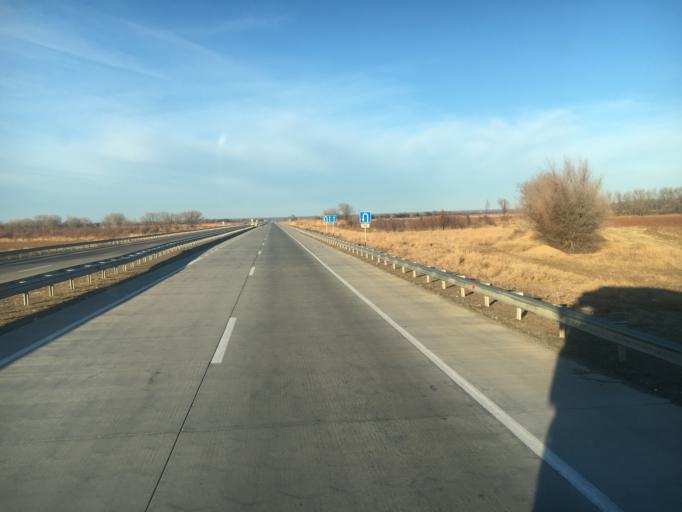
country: KZ
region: Ongtustik Qazaqstan
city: Turkestan
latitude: 43.1557
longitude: 68.5636
